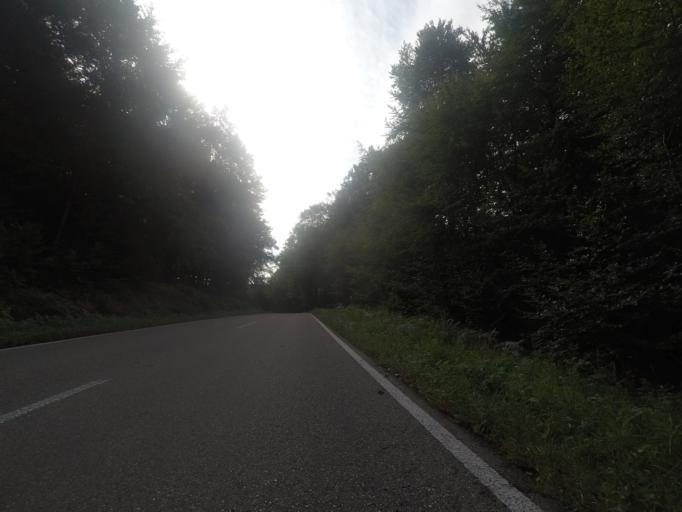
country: DE
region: Baden-Wuerttemberg
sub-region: Karlsruhe Region
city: Malsch
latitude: 48.8507
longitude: 8.3582
